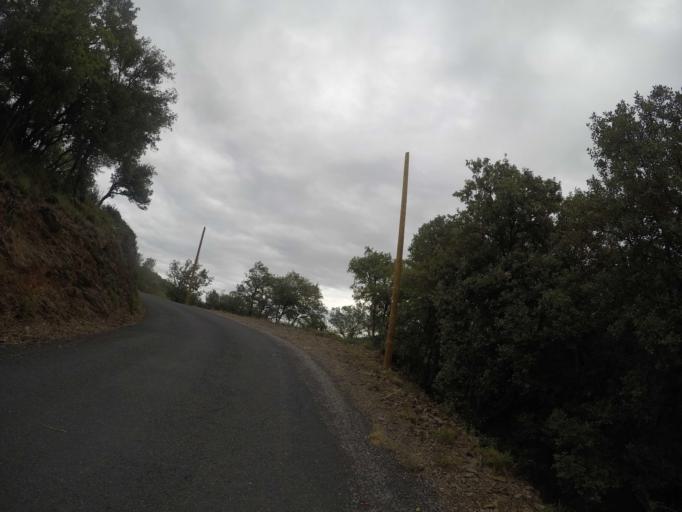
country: FR
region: Languedoc-Roussillon
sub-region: Departement des Pyrenees-Orientales
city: Ille-sur-Tet
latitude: 42.6336
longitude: 2.6183
